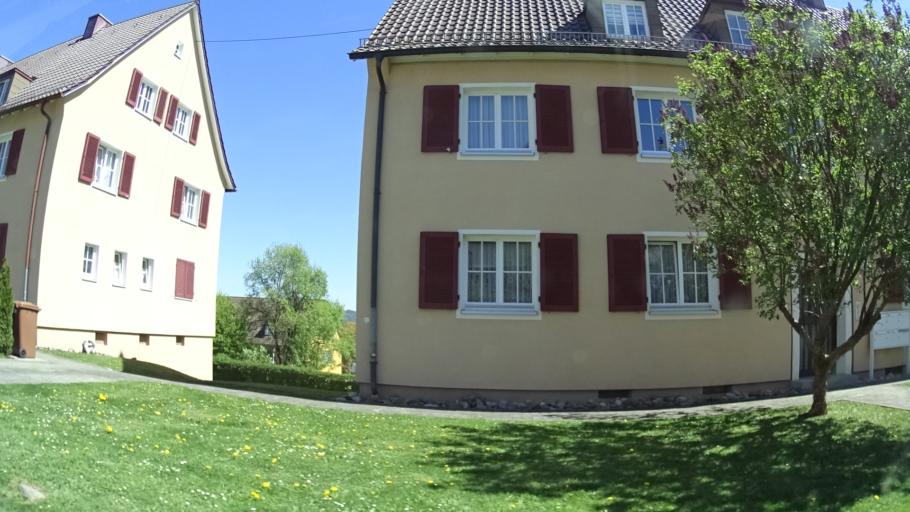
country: DE
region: Baden-Wuerttemberg
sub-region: Freiburg Region
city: Rottweil
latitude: 48.1724
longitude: 8.6253
